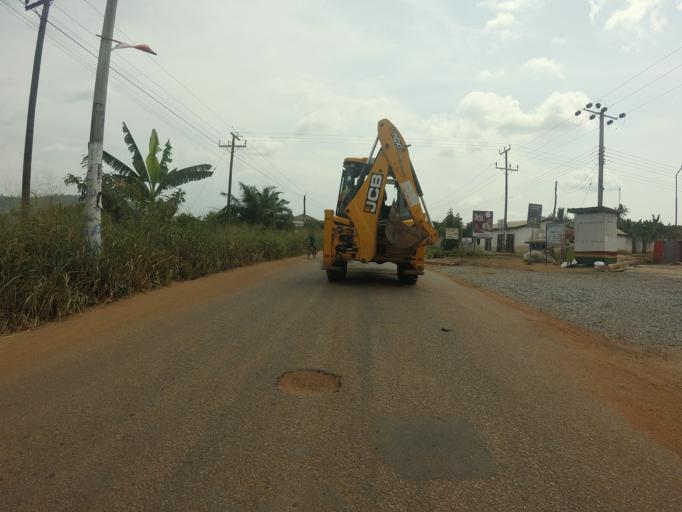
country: GH
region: Eastern
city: Koforidua
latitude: 6.0419
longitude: -0.2607
